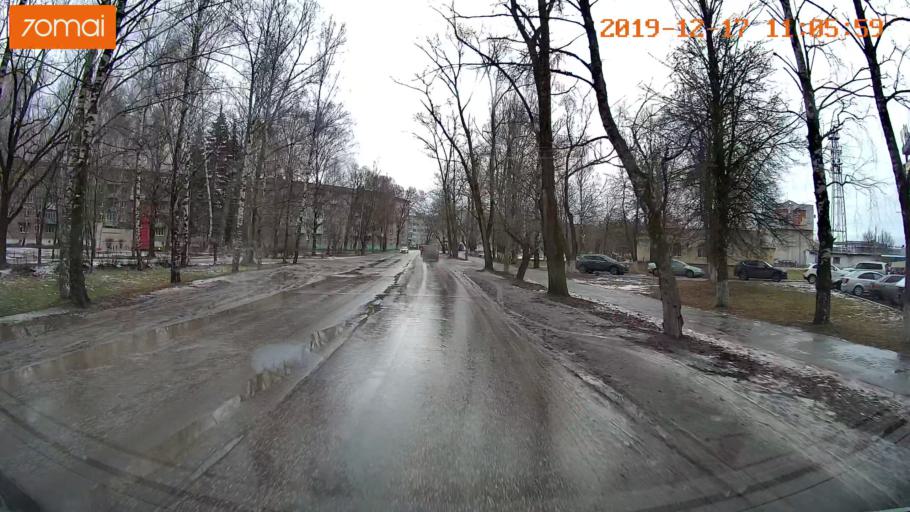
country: RU
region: Vladimir
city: Gus'-Khrustal'nyy
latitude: 55.6177
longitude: 40.6433
